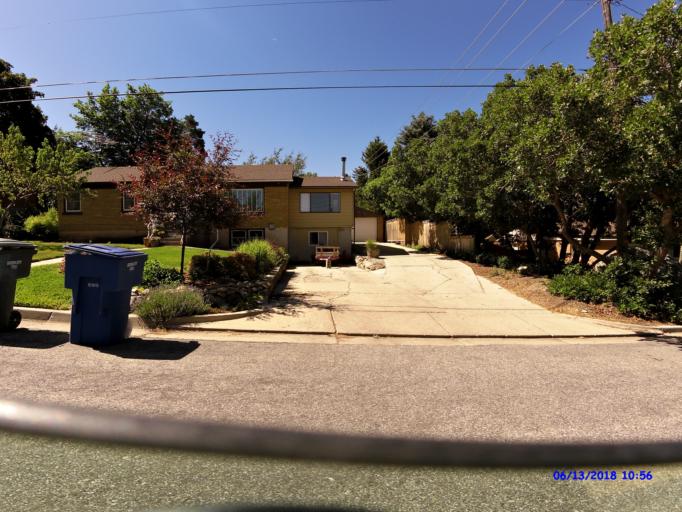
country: US
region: Utah
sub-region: Weber County
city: South Ogden
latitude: 41.2014
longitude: -111.9384
